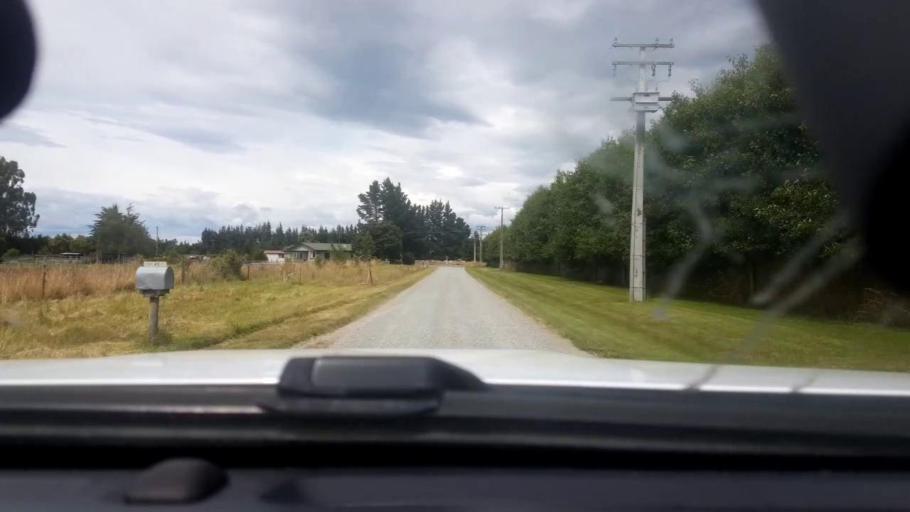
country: NZ
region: Canterbury
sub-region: Timaru District
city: Pleasant Point
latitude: -44.1432
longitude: 171.2890
